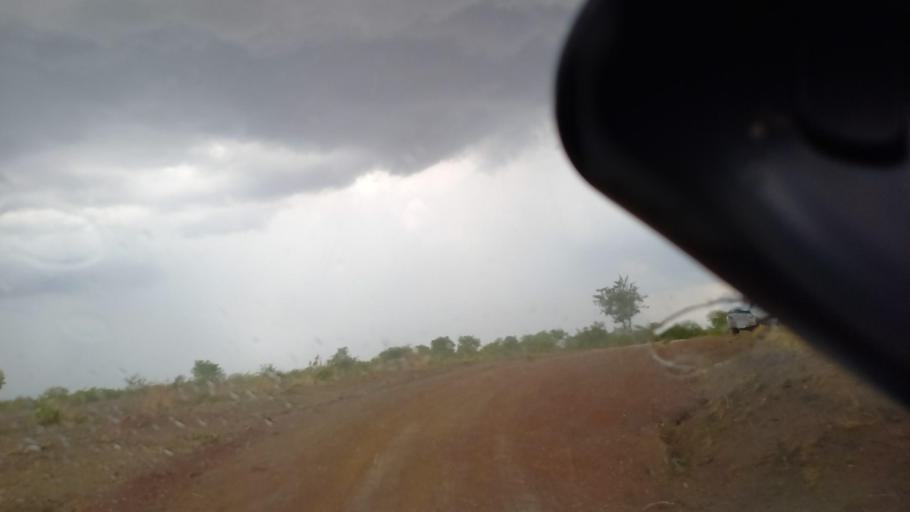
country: ZM
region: Lusaka
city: Kafue
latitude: -15.8642
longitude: 28.1788
